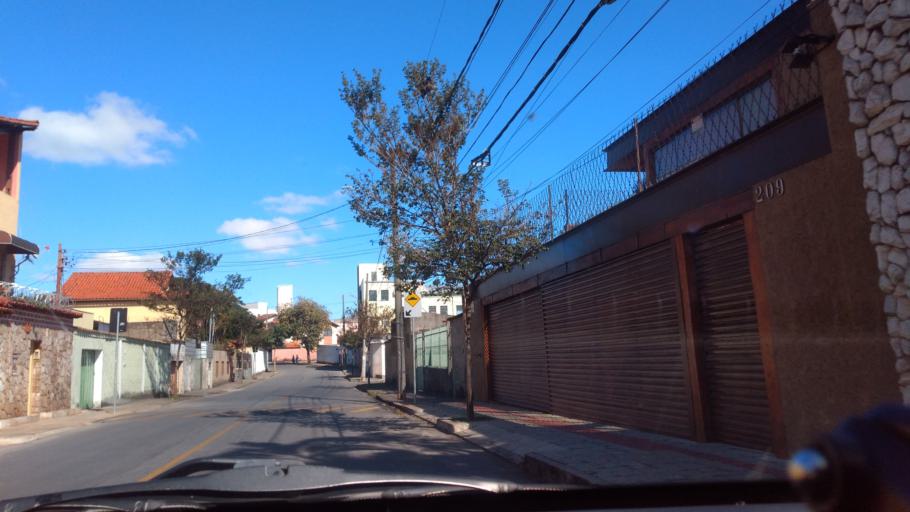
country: BR
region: Minas Gerais
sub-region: Belo Horizonte
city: Belo Horizonte
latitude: -19.8395
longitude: -43.9479
